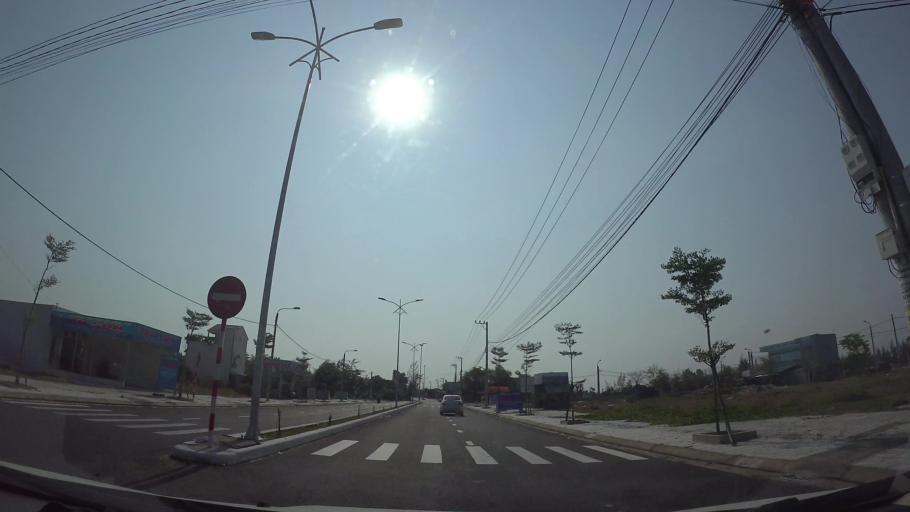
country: VN
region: Da Nang
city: Ngu Hanh Son
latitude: 15.9540
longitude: 108.2802
